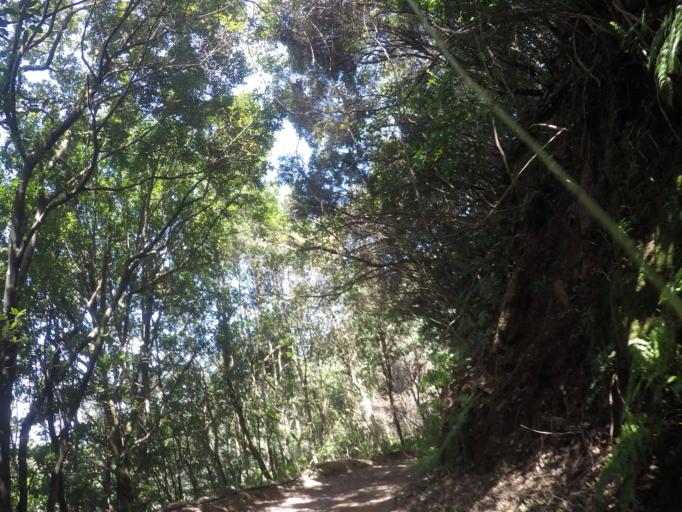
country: ES
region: Canary Islands
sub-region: Provincia de Santa Cruz de Tenerife
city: Santa Cruz de Tenerife
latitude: 28.5437
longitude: -16.2271
